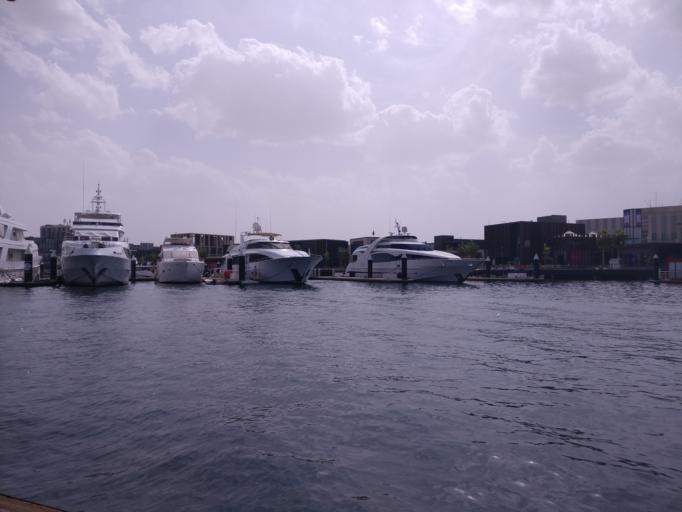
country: AE
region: Ash Shariqah
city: Sharjah
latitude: 25.2603
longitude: 55.3109
